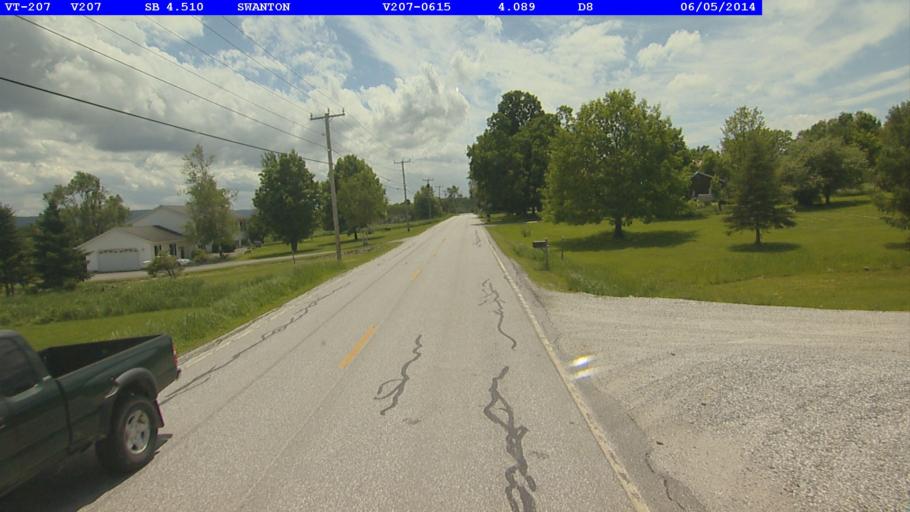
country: US
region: Vermont
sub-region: Franklin County
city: Swanton
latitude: 44.9028
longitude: -73.0650
